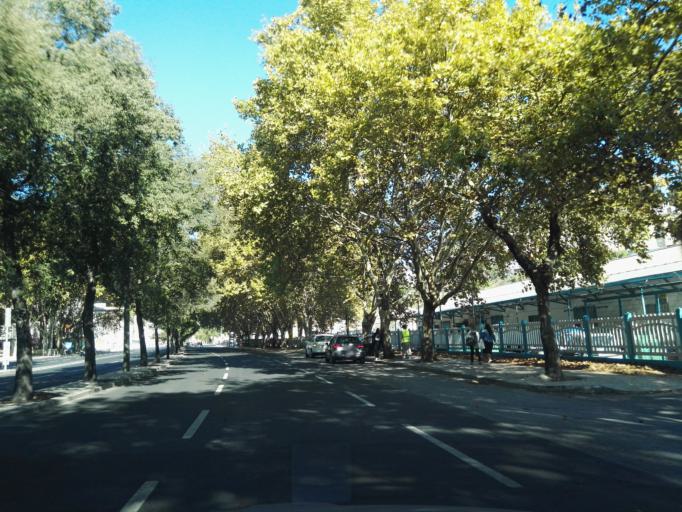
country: PT
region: Setubal
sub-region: Almada
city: Cacilhas
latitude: 38.7093
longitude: -9.1737
